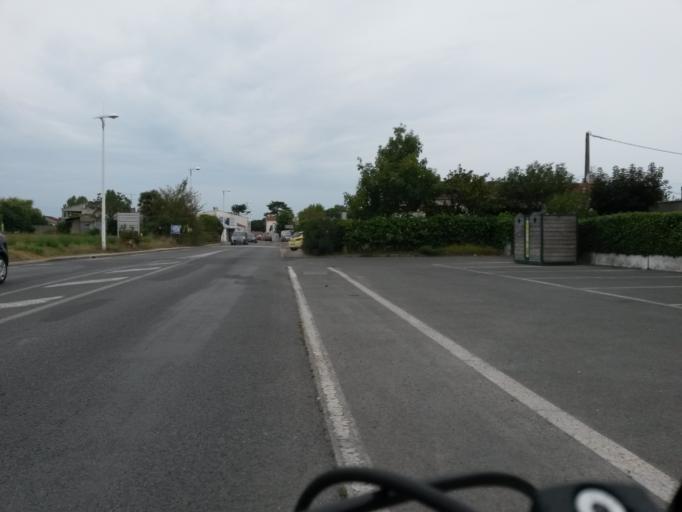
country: FR
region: Poitou-Charentes
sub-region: Departement de la Charente-Maritime
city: Dolus-d'Oleron
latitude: 45.9412
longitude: -1.3139
